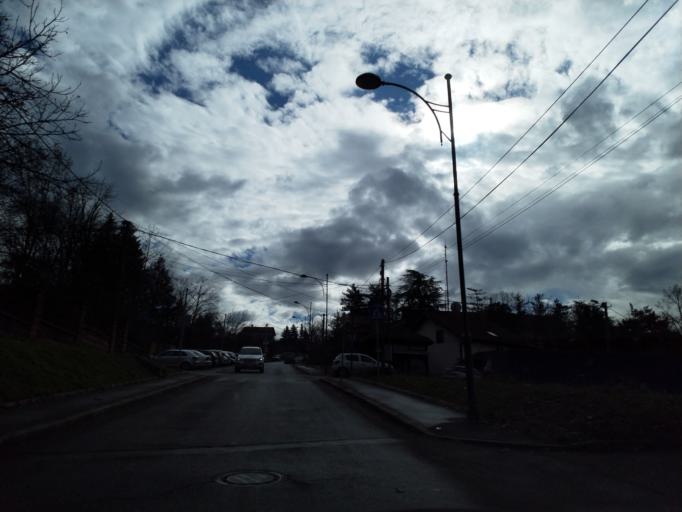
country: RS
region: Central Serbia
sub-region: Belgrade
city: Grocka
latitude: 44.6684
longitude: 20.7197
